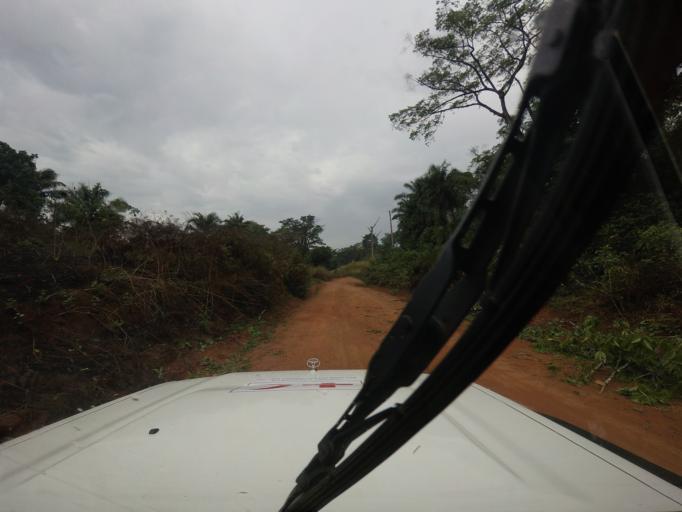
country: SL
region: Eastern Province
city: Buedu
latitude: 8.3207
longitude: -10.1556
